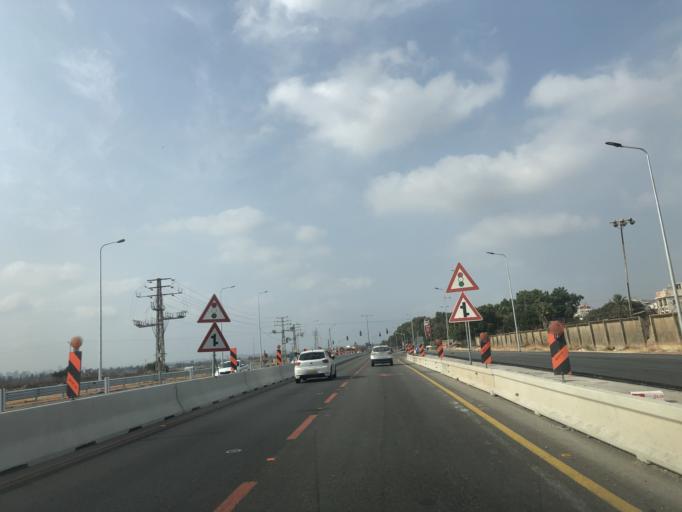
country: IL
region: Central District
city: Rosh Ha'Ayin
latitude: 32.0916
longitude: 34.9420
